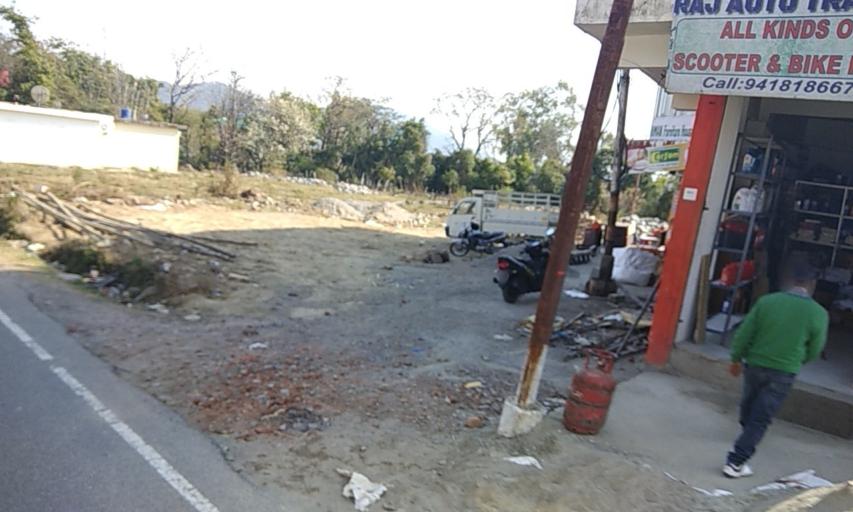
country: IN
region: Himachal Pradesh
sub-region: Kangra
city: Dharmsala
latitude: 32.1641
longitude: 76.3987
